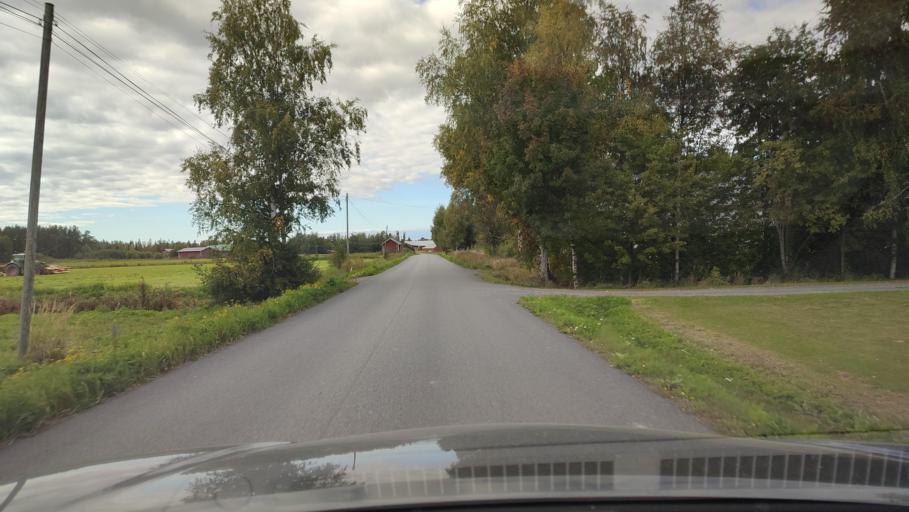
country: FI
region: Southern Ostrobothnia
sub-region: Suupohja
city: Karijoki
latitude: 62.2374
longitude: 21.5884
